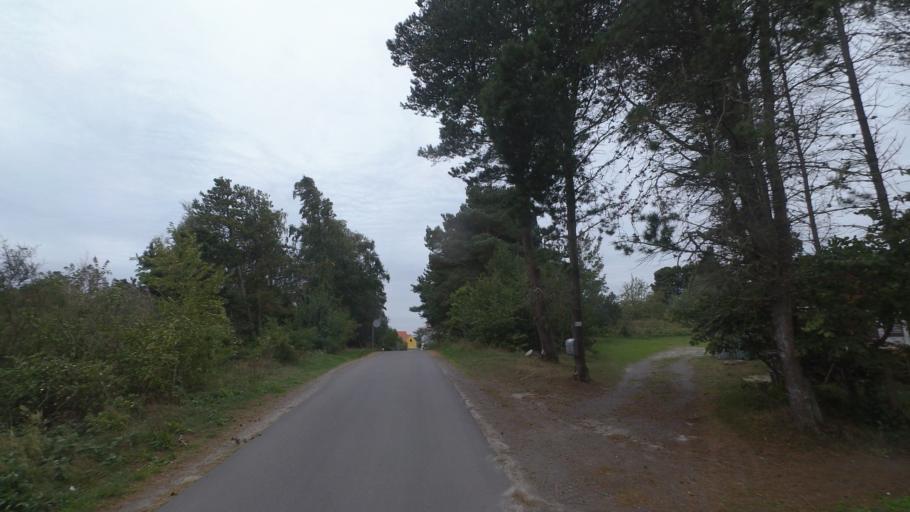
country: DK
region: Capital Region
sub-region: Bornholm Kommune
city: Akirkeby
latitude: 55.0025
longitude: 14.9917
